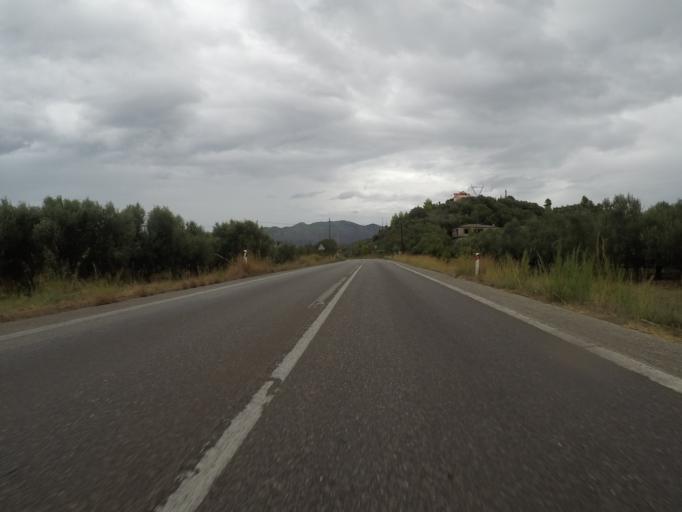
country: GR
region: West Greece
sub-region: Nomos Ileias
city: Zacharo
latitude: 37.4568
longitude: 21.6595
